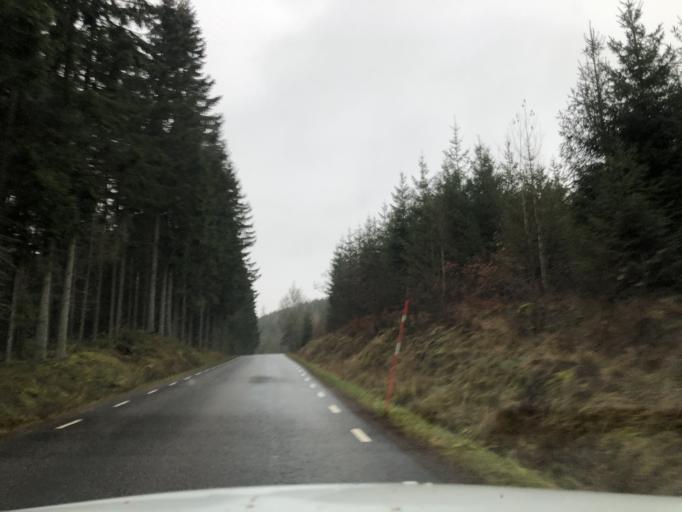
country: SE
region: Vaestra Goetaland
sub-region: Ulricehamns Kommun
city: Ulricehamn
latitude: 57.8308
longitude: 13.4077
